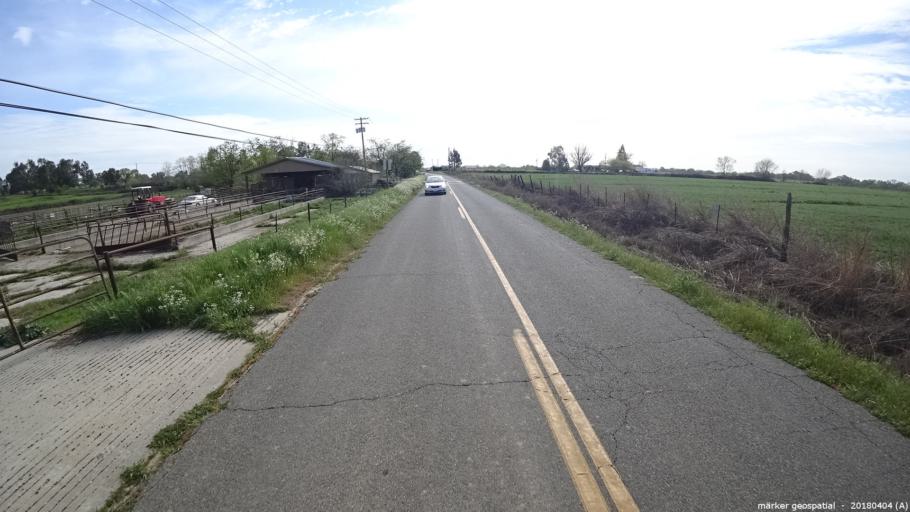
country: US
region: California
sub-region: Sacramento County
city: Herald
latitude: 38.2553
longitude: -121.2466
